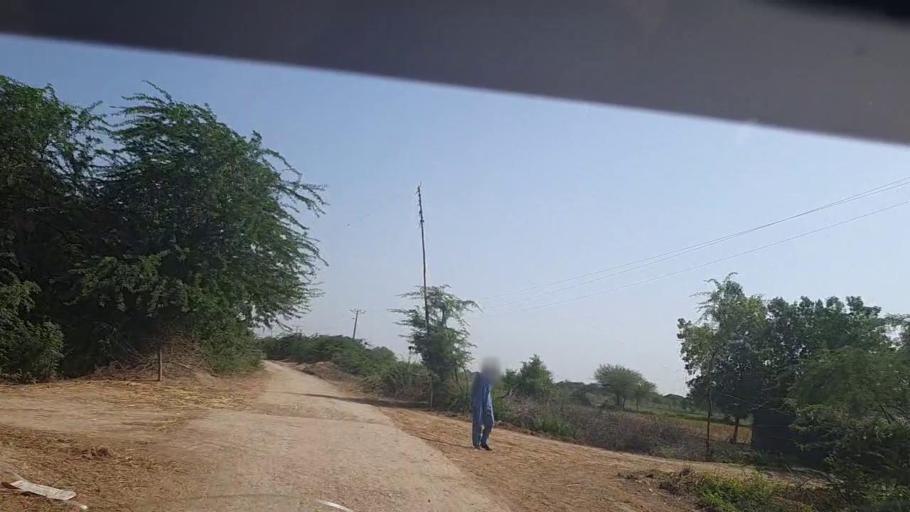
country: PK
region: Sindh
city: Rajo Khanani
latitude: 24.9617
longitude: 68.8917
